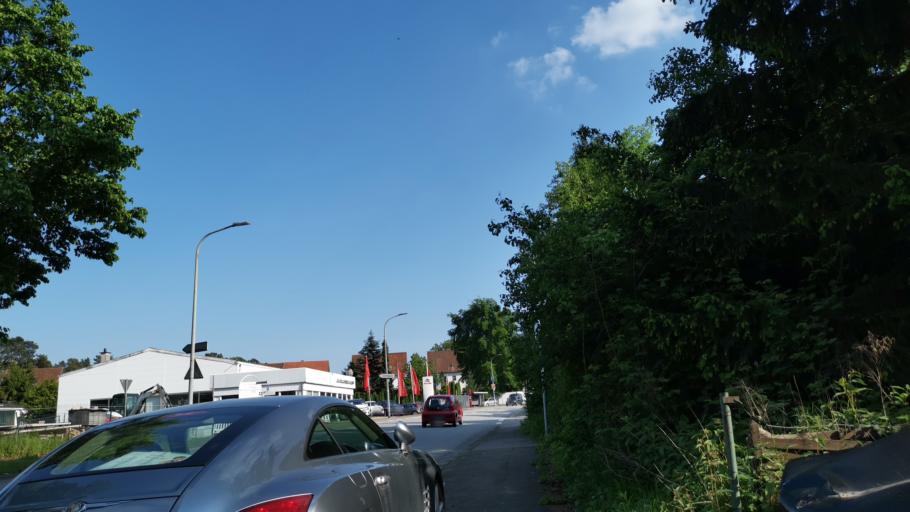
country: DE
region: Saarland
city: Sankt Ingbert
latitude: 49.2716
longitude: 7.1620
